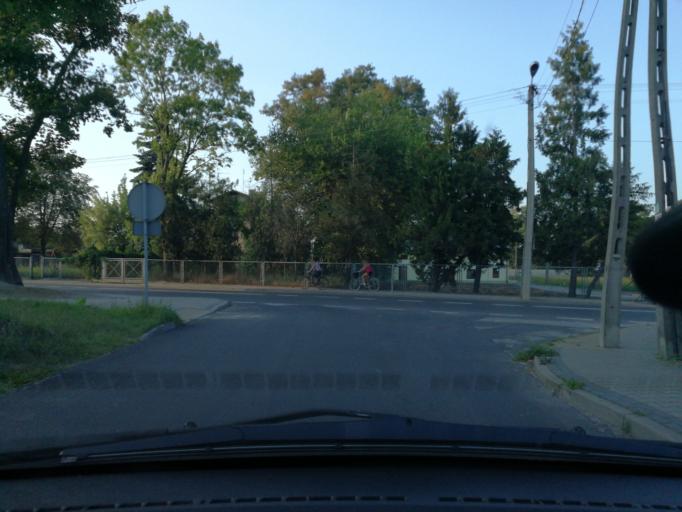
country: PL
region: Lodz Voivodeship
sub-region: Skierniewice
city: Skierniewice
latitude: 51.9607
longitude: 20.1359
